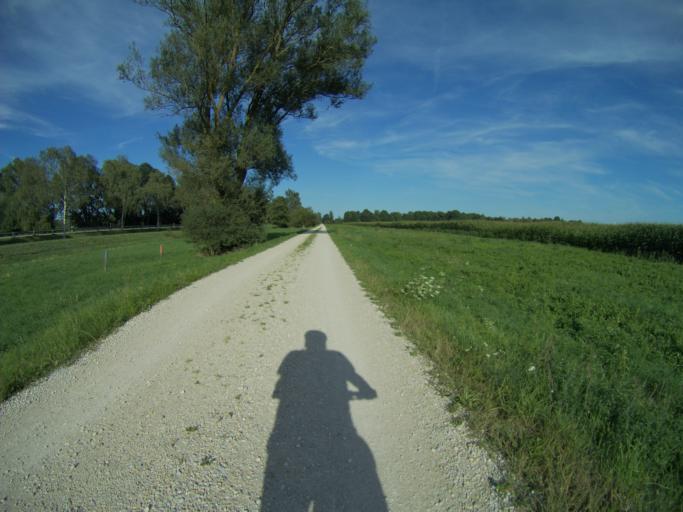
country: DE
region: Bavaria
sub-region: Upper Bavaria
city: Marzling
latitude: 48.3741
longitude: 11.8226
